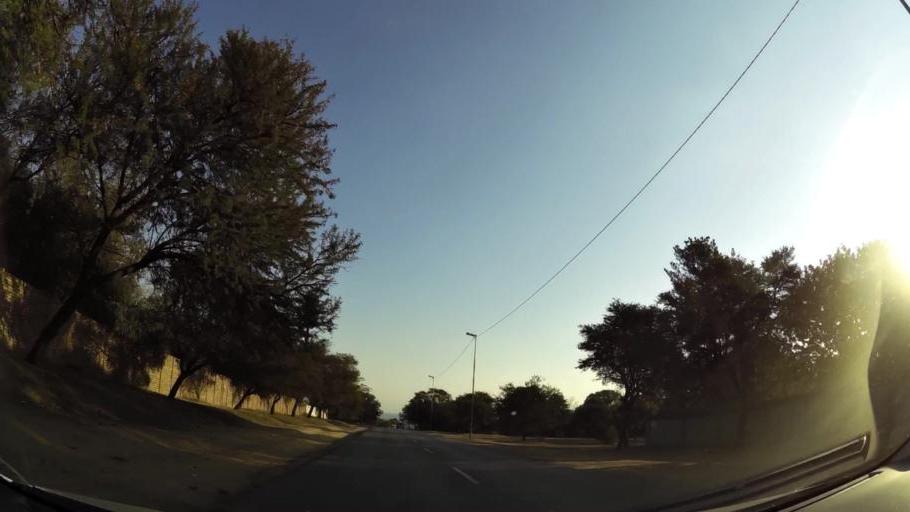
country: ZA
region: Gauteng
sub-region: City of Johannesburg Metropolitan Municipality
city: Midrand
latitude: -26.0245
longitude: 28.1505
